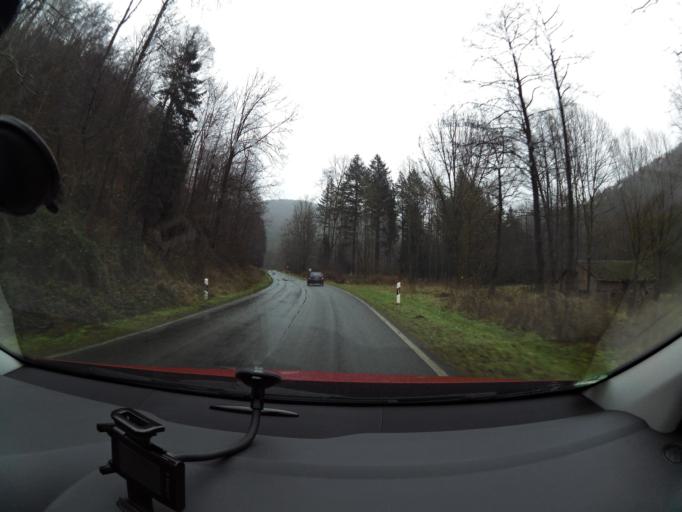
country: DE
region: Lower Saxony
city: Herzberg am Harz
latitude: 51.6803
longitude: 10.3942
